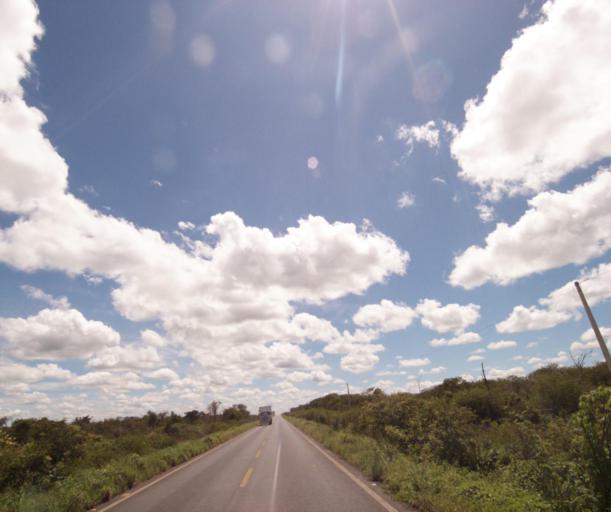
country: BR
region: Bahia
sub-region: Sao Felix Do Coribe
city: Santa Maria da Vitoria
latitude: -13.3415
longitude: -43.9171
